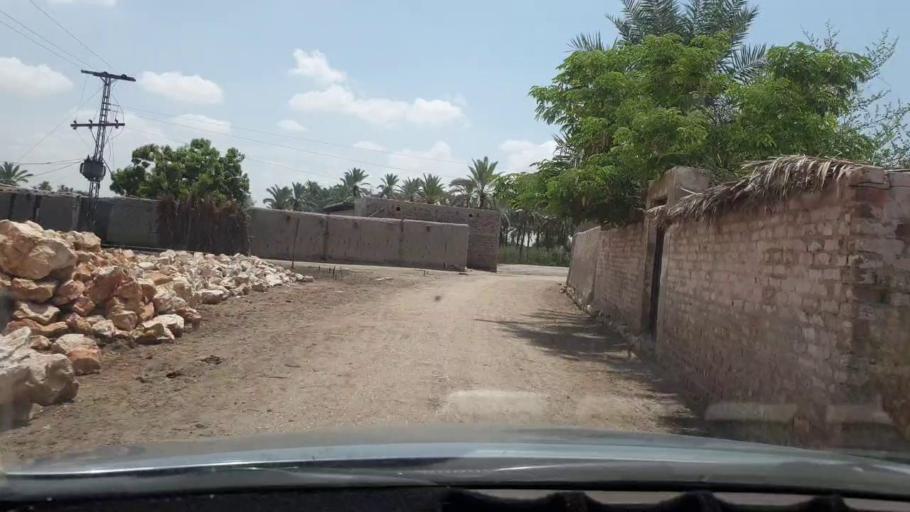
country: PK
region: Sindh
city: Khairpur
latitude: 27.4427
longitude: 68.7919
